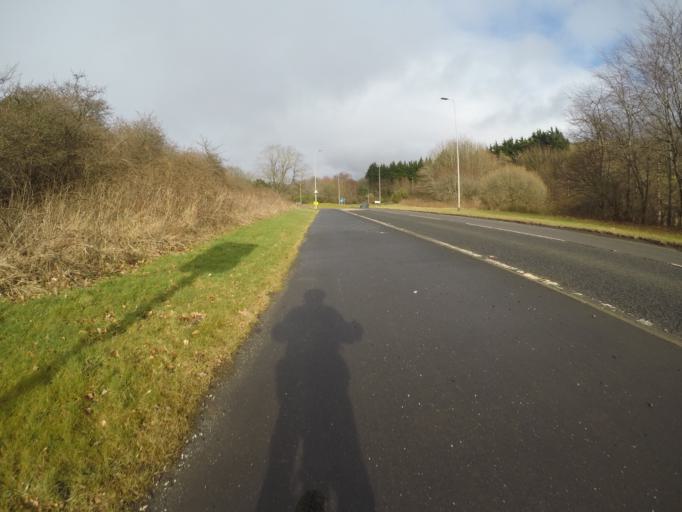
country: GB
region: Scotland
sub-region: North Ayrshire
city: Fairlie
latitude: 55.7428
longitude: -4.8591
